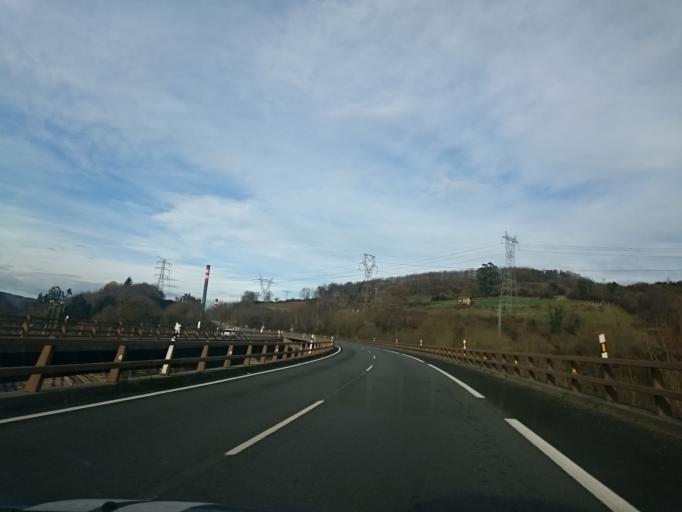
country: ES
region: Asturias
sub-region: Province of Asturias
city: Castandiello
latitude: 43.3097
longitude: -5.8641
